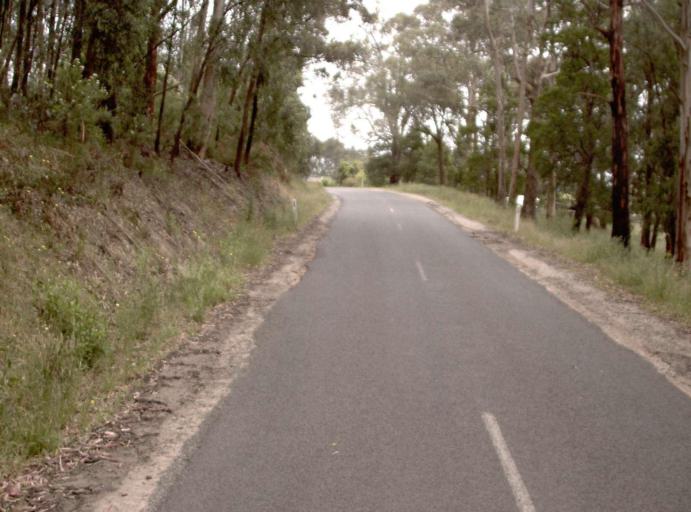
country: AU
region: Victoria
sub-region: Latrobe
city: Moe
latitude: -37.9837
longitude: 146.1436
